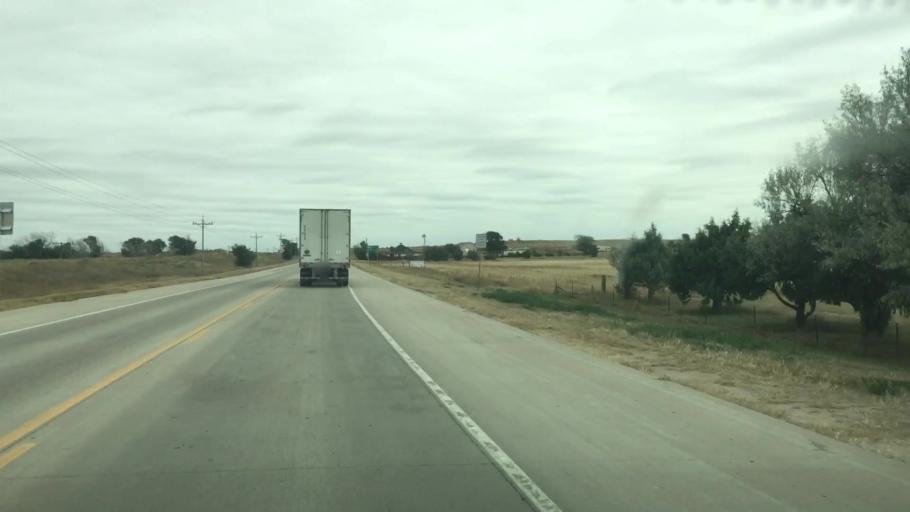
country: US
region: Colorado
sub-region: Kiowa County
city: Eads
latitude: 38.4772
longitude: -102.7711
